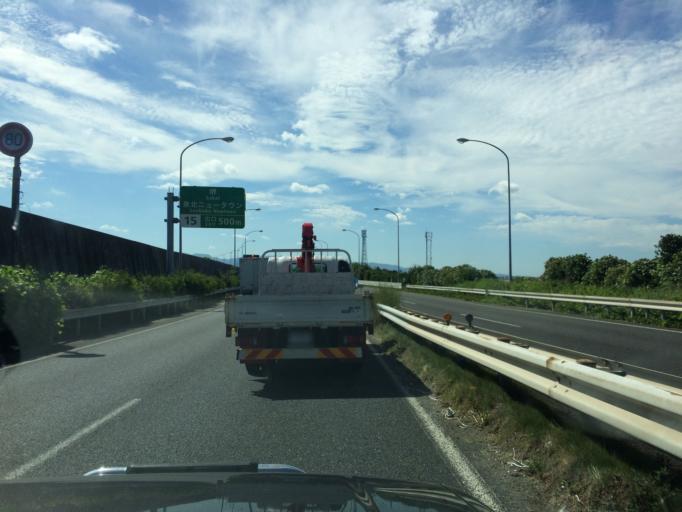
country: JP
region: Osaka
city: Takaishi
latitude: 34.5173
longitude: 135.4906
